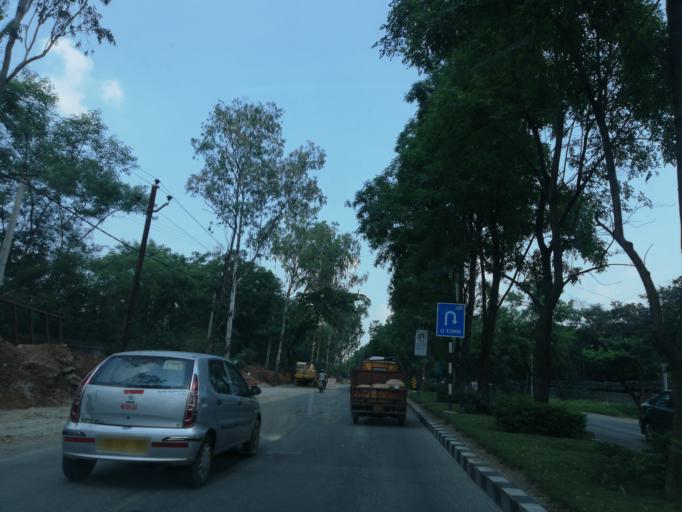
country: IN
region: Telangana
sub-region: Medak
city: Serilingampalle
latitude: 17.4536
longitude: 78.3428
